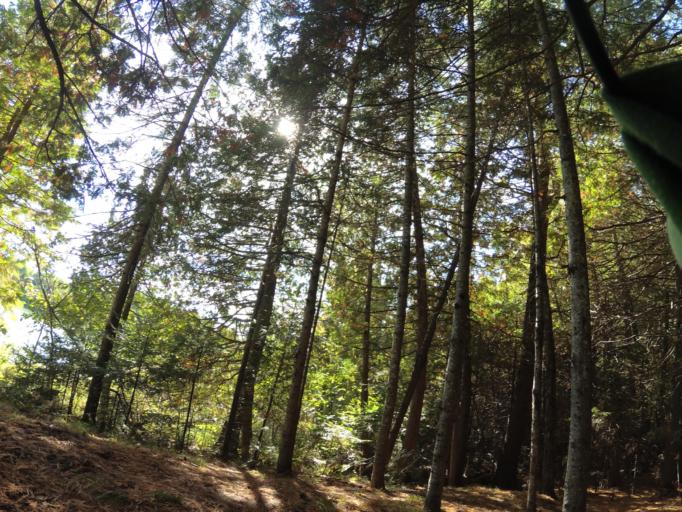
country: CA
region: Ontario
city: Pembroke
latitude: 45.3495
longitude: -77.1637
